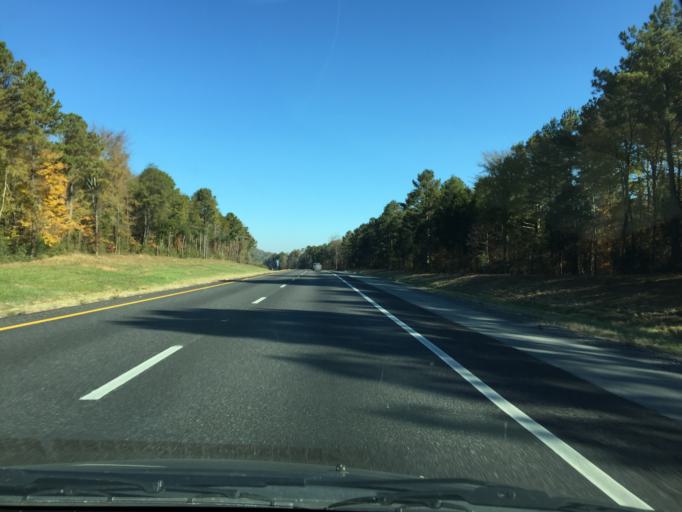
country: US
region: Tennessee
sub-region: Meigs County
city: Decatur
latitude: 35.3602
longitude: -84.7403
